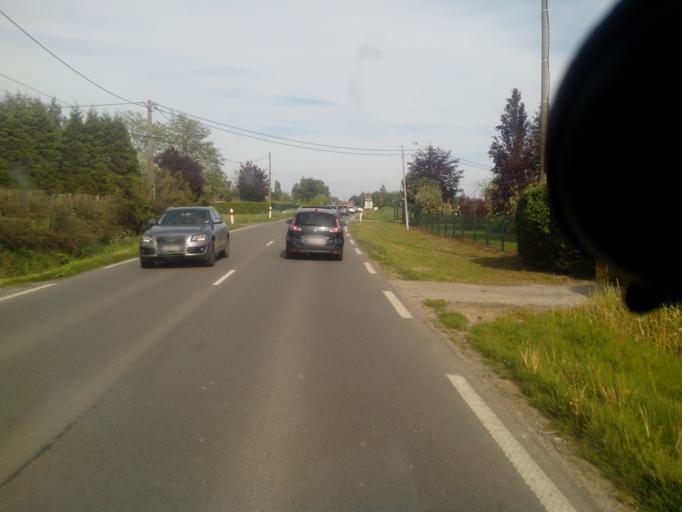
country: FR
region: Nord-Pas-de-Calais
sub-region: Departement du Nord
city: Steenbecque
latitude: 50.7302
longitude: 2.4641
